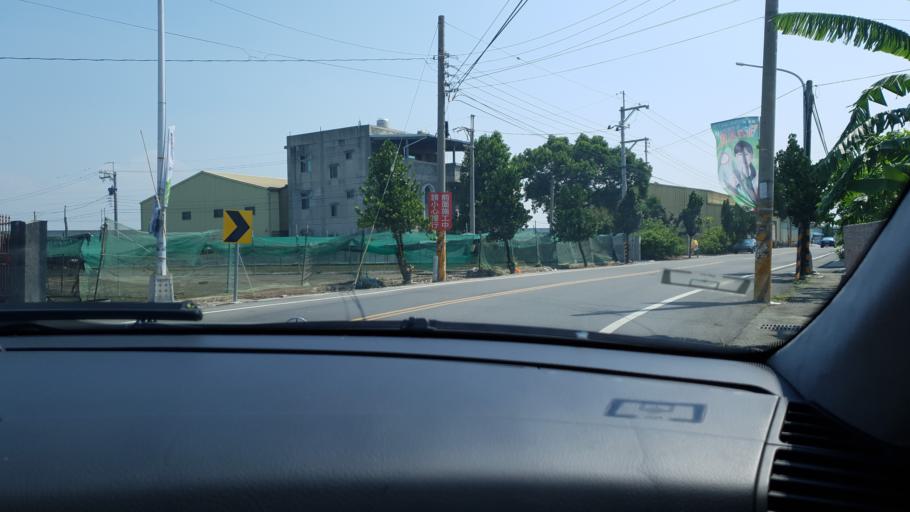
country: TW
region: Taiwan
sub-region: Yunlin
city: Douliu
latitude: 23.7568
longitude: 120.4207
